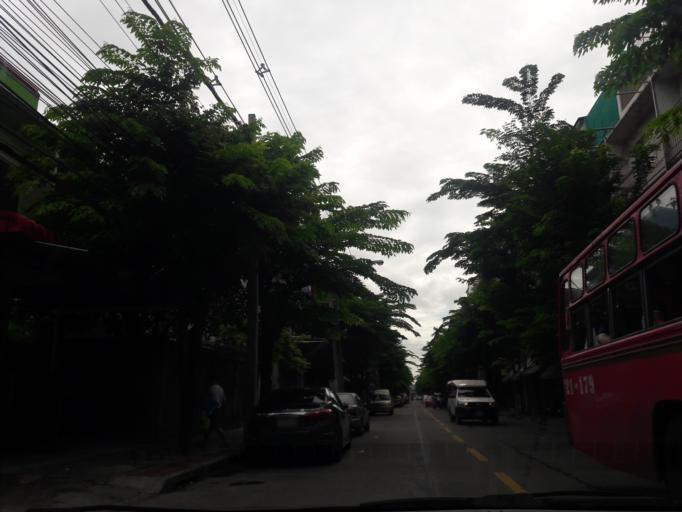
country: TH
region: Bangkok
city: Khlong San
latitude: 13.7261
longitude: 100.4982
